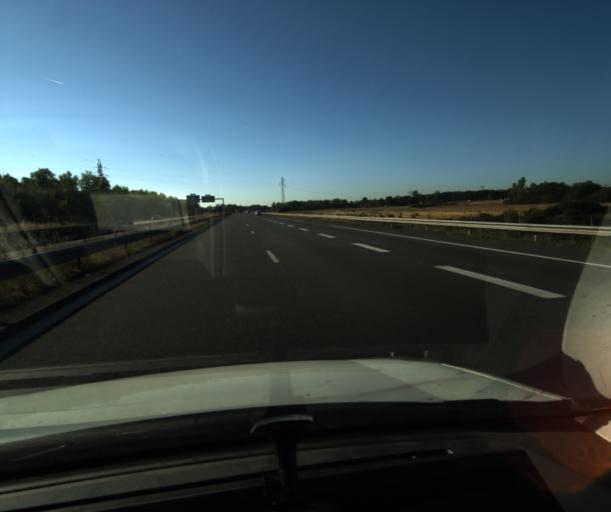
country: FR
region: Midi-Pyrenees
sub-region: Departement du Tarn-et-Garonne
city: Campsas
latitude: 43.9267
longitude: 1.3105
